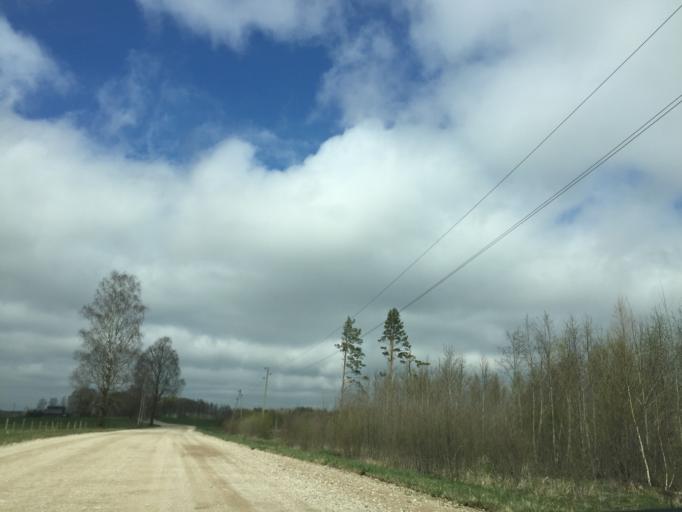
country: EE
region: Valgamaa
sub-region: Valga linn
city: Valga
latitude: 57.5576
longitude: 26.2808
